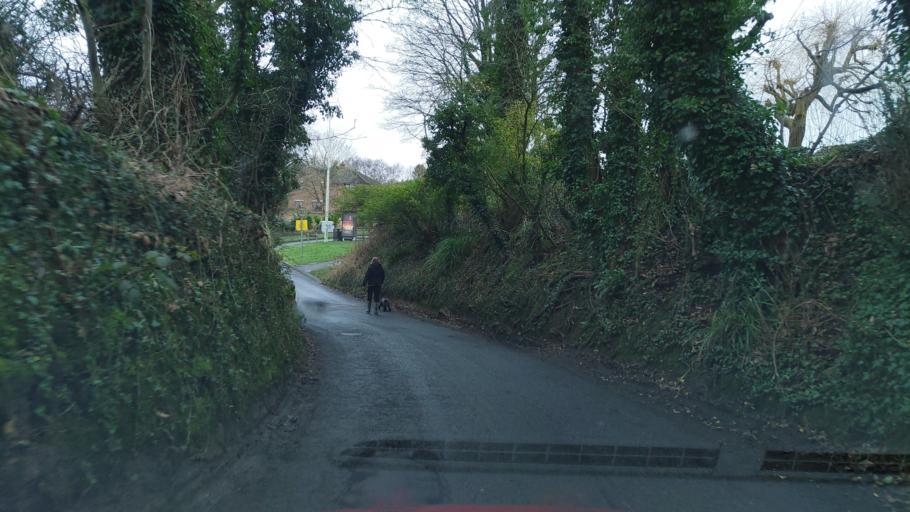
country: GB
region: England
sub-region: Lancashire
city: Clayton-le-Woods
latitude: 53.6995
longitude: -2.6604
